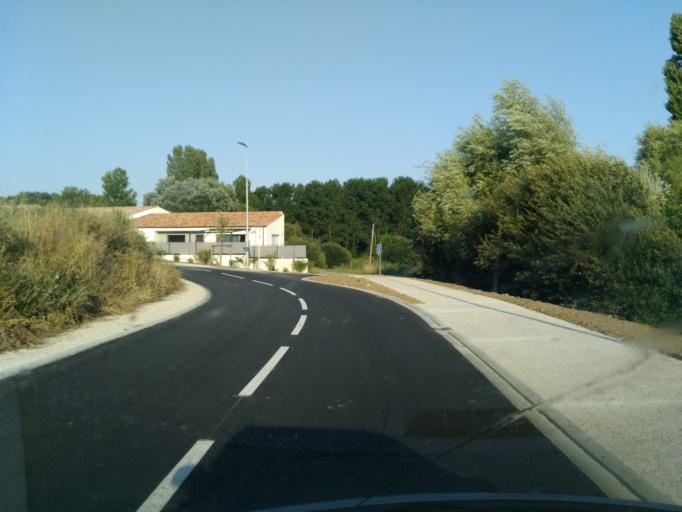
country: FR
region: Poitou-Charentes
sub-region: Departement de la Charente-Maritime
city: Vaux-sur-Mer
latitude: 45.6375
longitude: -1.0565
